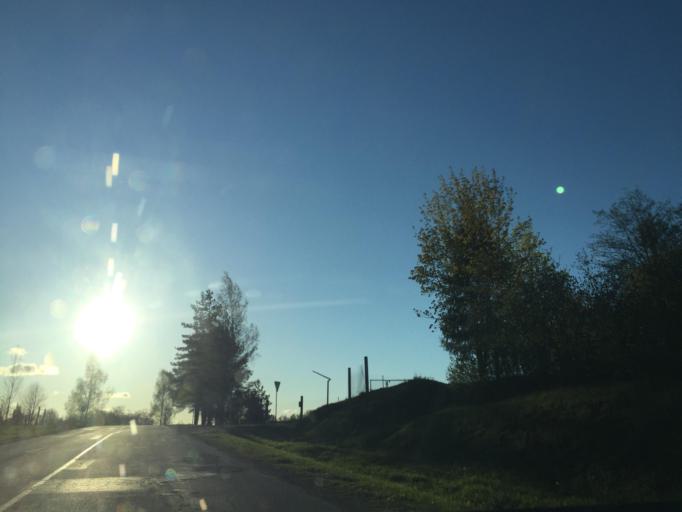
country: LV
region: Vecpiebalga
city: Vecpiebalga
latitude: 56.8658
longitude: 25.8406
